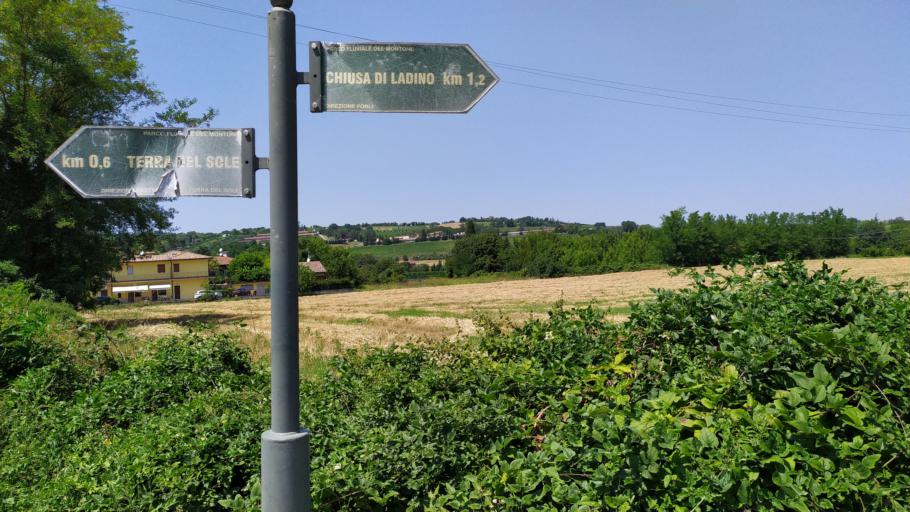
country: IT
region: Emilia-Romagna
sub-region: Forli-Cesena
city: Castrocaro Terme e Terra del Sole
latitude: 44.1869
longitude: 11.9638
